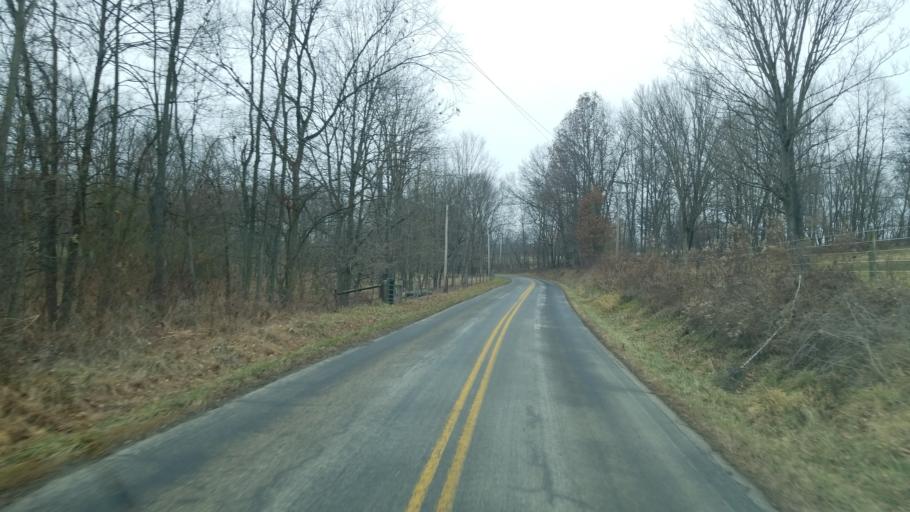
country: US
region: Ohio
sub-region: Holmes County
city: Millersburg
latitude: 40.4881
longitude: -81.8712
